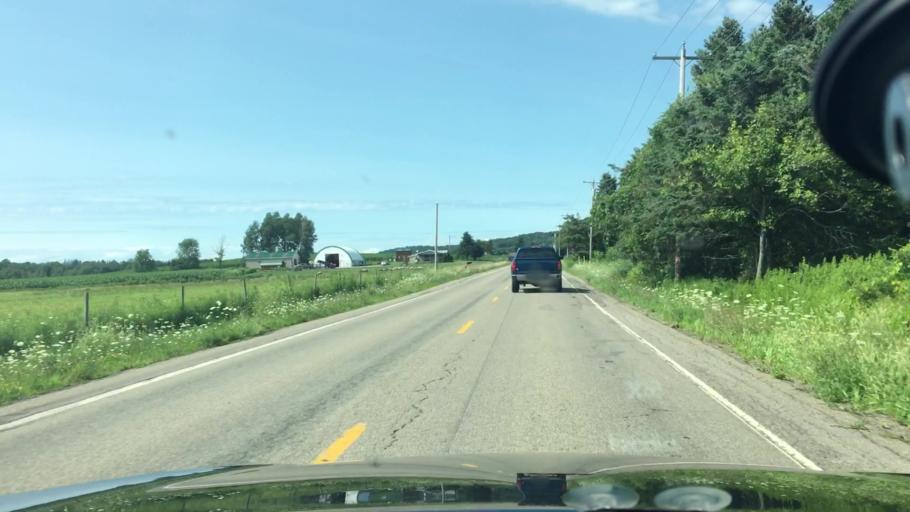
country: US
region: New York
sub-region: Chautauqua County
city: Brocton
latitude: 42.2990
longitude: -79.3531
